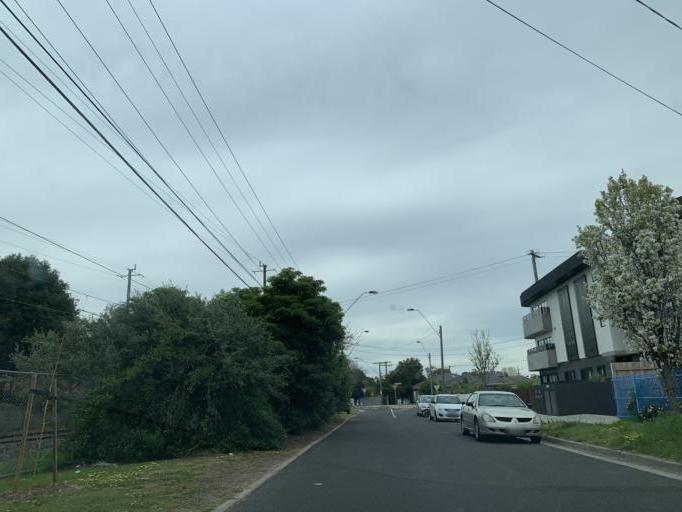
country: AU
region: Victoria
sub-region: Bayside
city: Highett
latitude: -37.9455
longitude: 145.0400
